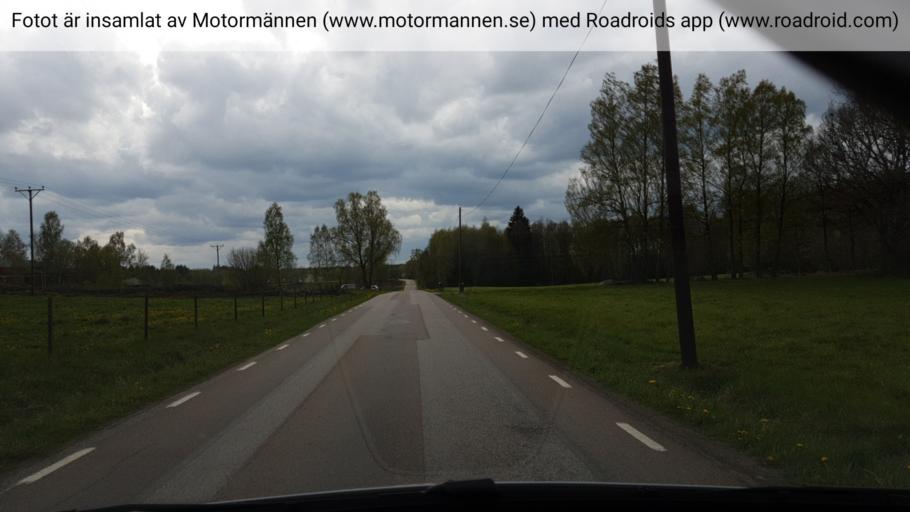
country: SE
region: Vaestra Goetaland
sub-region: Falkopings Kommun
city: Floby
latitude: 58.1652
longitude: 13.3407
